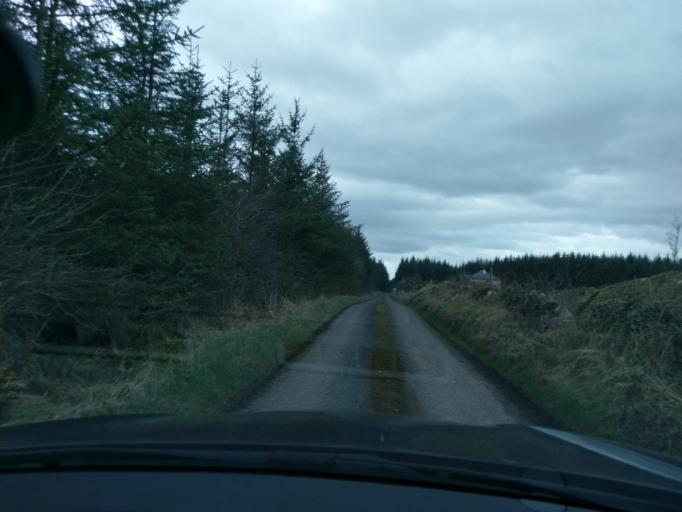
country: IE
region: Connaught
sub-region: County Galway
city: Athenry
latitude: 53.3793
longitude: -8.6359
